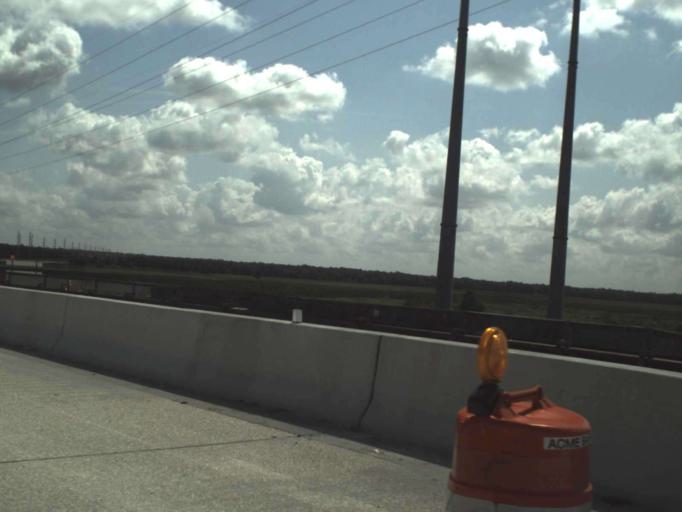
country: US
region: Florida
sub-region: Seminole County
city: Midway
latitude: 28.8034
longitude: -81.2101
